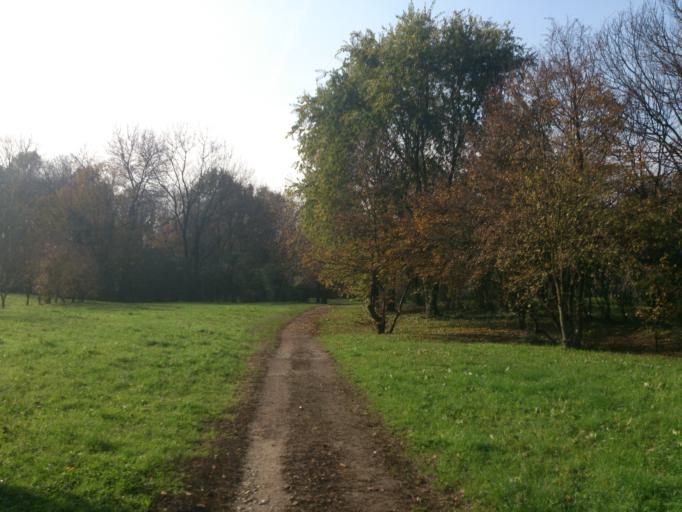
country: IT
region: Lombardy
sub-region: Citta metropolitana di Milano
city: San Donato Milanese
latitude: 45.4240
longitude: 9.2726
